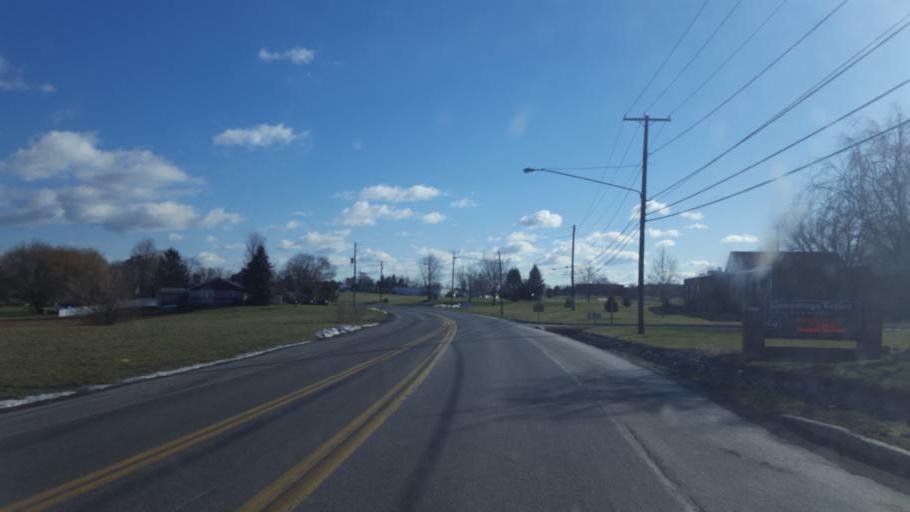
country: US
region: Pennsylvania
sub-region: Lancaster County
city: Lampeter
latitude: 40.0517
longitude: -76.2221
